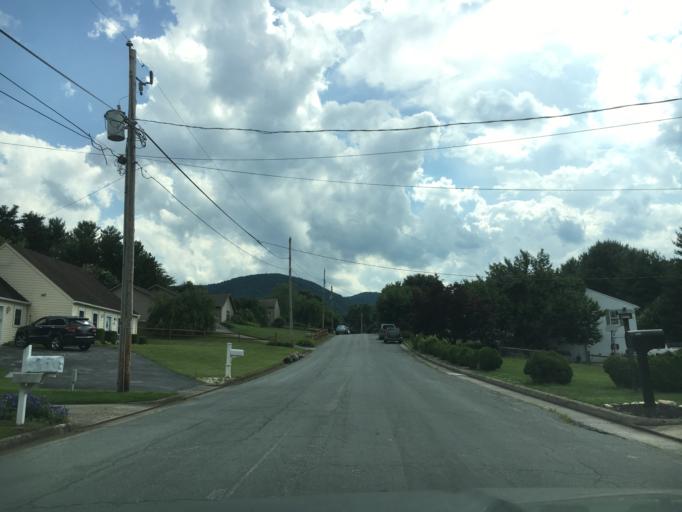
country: US
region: Virginia
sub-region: Roanoke County
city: Cave Spring
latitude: 37.2476
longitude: -80.0400
